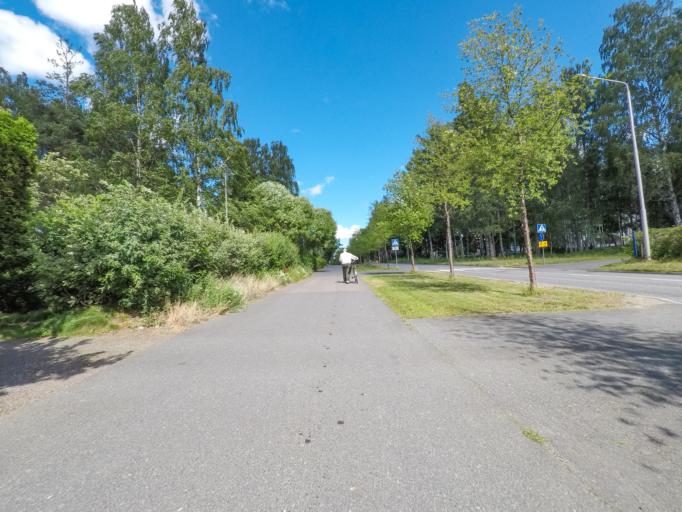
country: FI
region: South Karelia
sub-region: Lappeenranta
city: Lappeenranta
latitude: 61.0633
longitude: 28.2226
